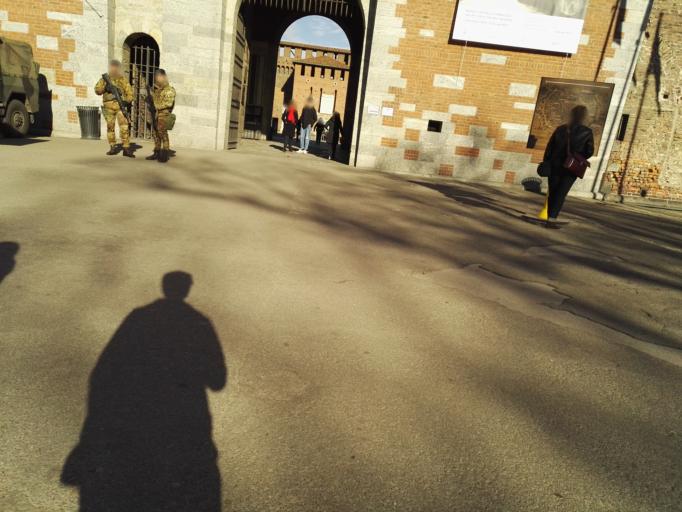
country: IT
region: Lombardy
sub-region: Citta metropolitana di Milano
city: Milano
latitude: 45.4697
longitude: 9.1804
